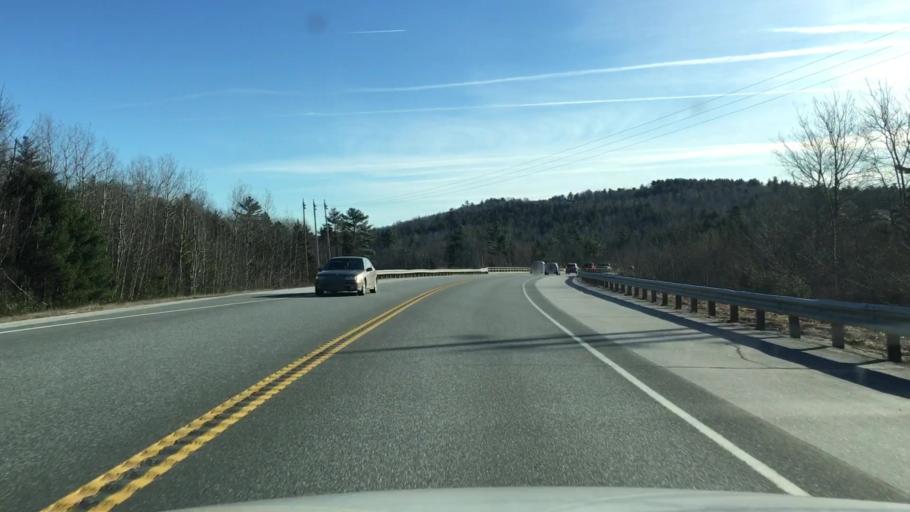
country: US
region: Maine
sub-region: Hancock County
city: Dedham
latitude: 44.6826
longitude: -68.5788
